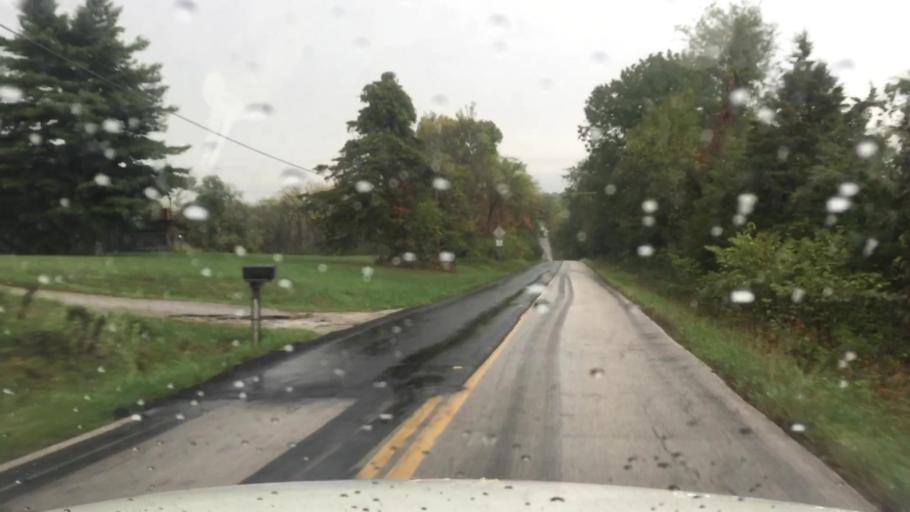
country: US
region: Missouri
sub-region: Boone County
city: Columbia
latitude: 38.9350
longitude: -92.4964
